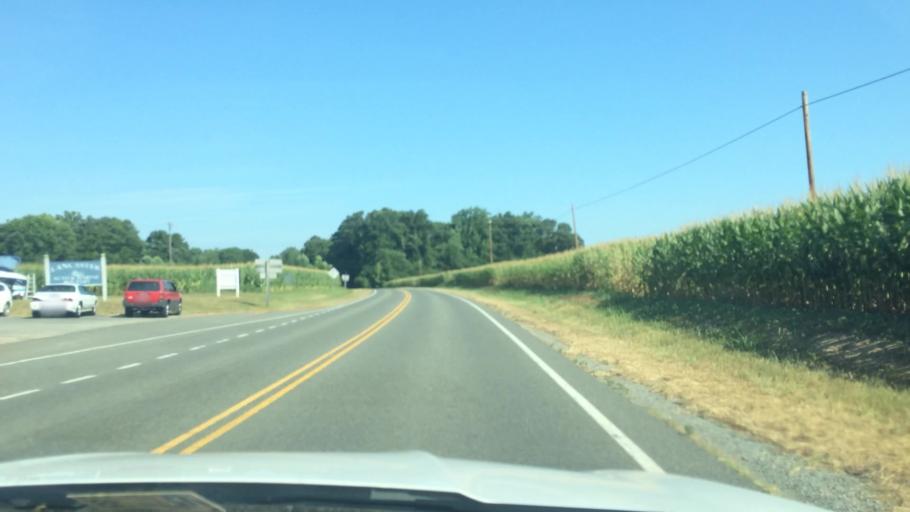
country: US
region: Virginia
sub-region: Lancaster County
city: Lancaster
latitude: 37.7960
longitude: -76.5218
